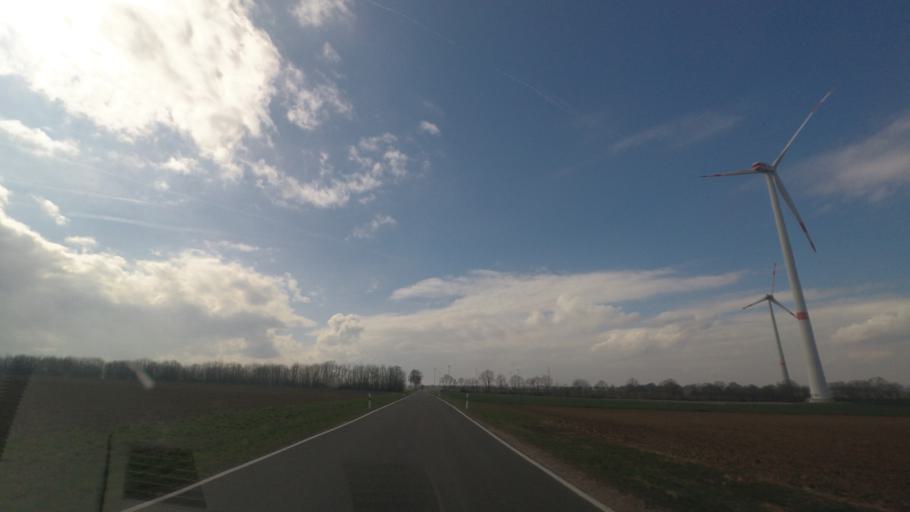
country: DE
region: Rheinland-Pfalz
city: Lonsheim
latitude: 49.7548
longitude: 8.0633
